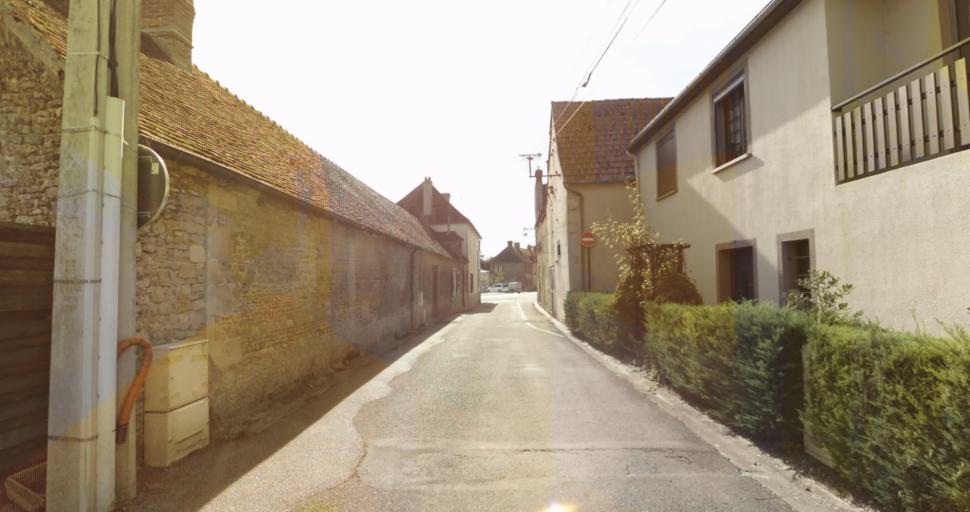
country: FR
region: Lower Normandy
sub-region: Departement de l'Orne
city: Gace
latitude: 48.7073
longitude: 0.2240
